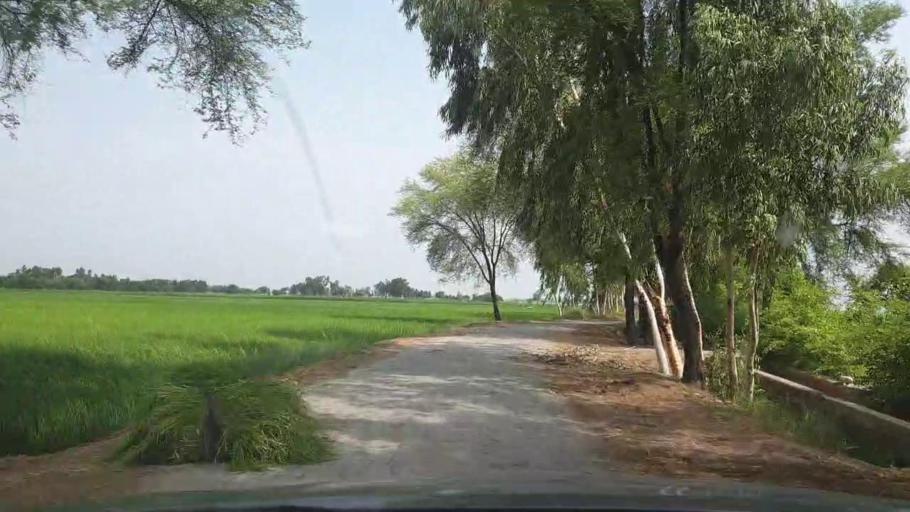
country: PK
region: Sindh
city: Ratodero
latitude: 27.8520
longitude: 68.2996
